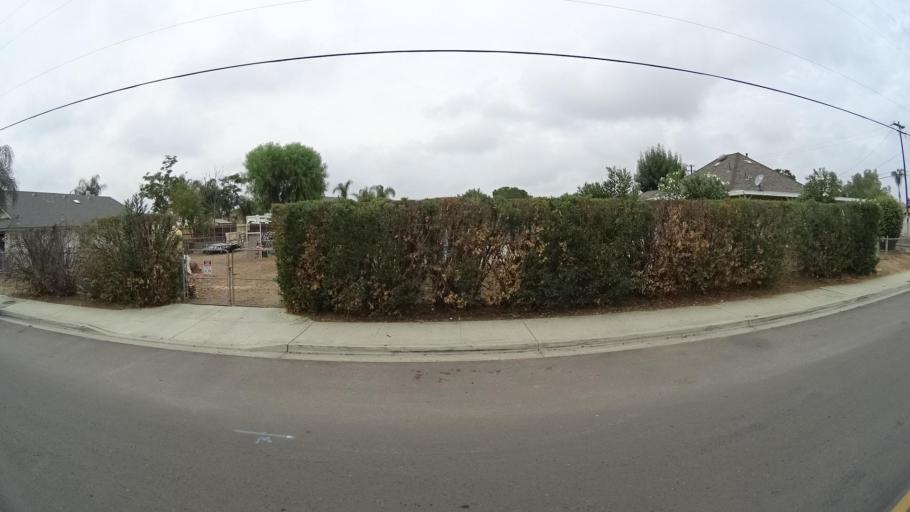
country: US
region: California
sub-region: San Diego County
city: Ramona
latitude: 33.0382
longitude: -116.8701
